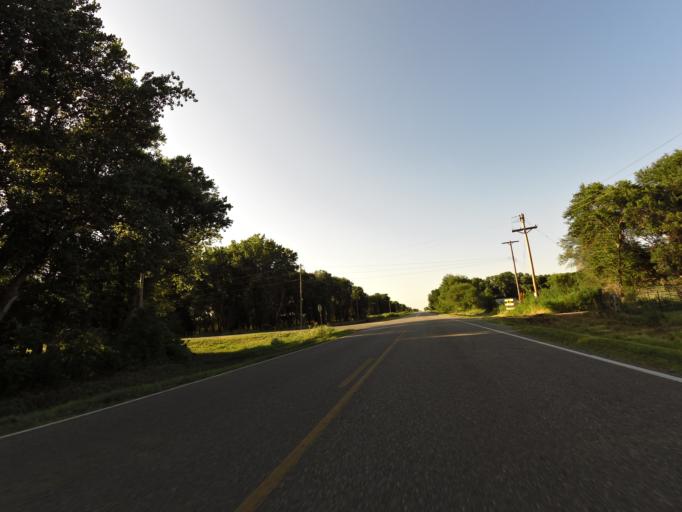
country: US
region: Kansas
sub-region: Reno County
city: Buhler
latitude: 38.1588
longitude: -97.8487
